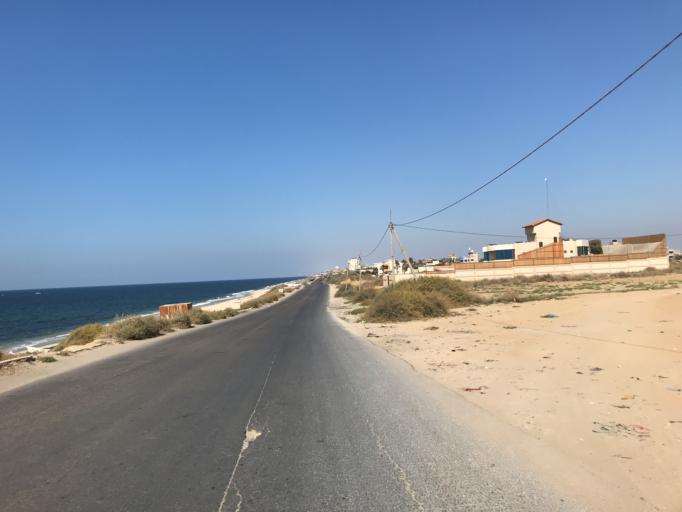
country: PS
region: Gaza Strip
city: Dayr al Balah
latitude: 31.4402
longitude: 34.3532
